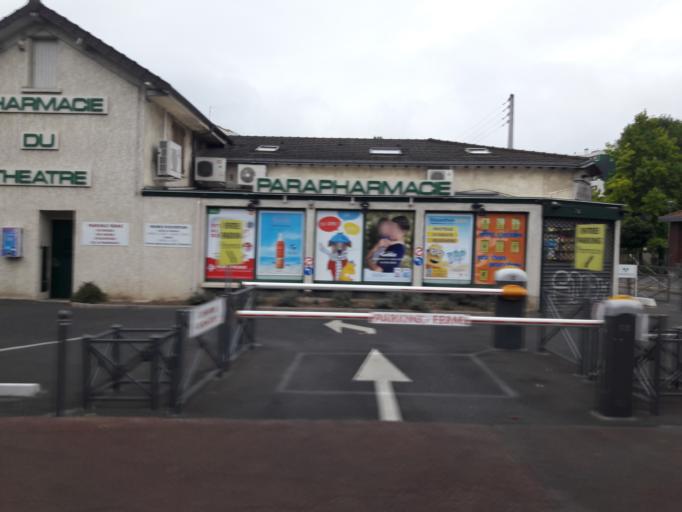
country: FR
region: Ile-de-France
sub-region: Departement de l'Essonne
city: Longjumeau
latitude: 48.6951
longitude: 2.2987
